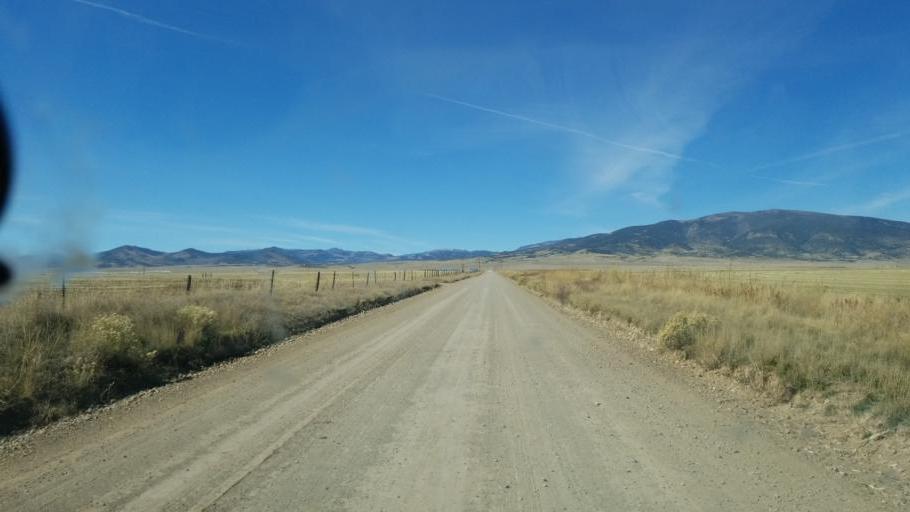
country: US
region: Colorado
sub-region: Rio Grande County
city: Monte Vista
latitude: 37.4011
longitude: -106.1249
